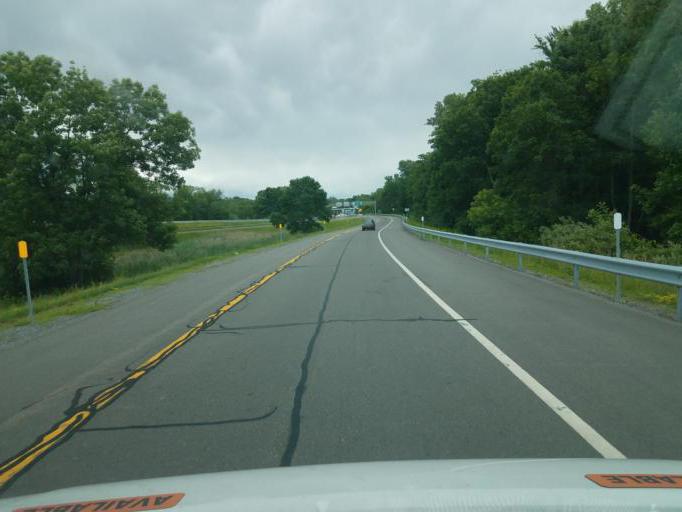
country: US
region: New York
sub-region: Ontario County
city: Phelps
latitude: 42.9541
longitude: -76.9835
